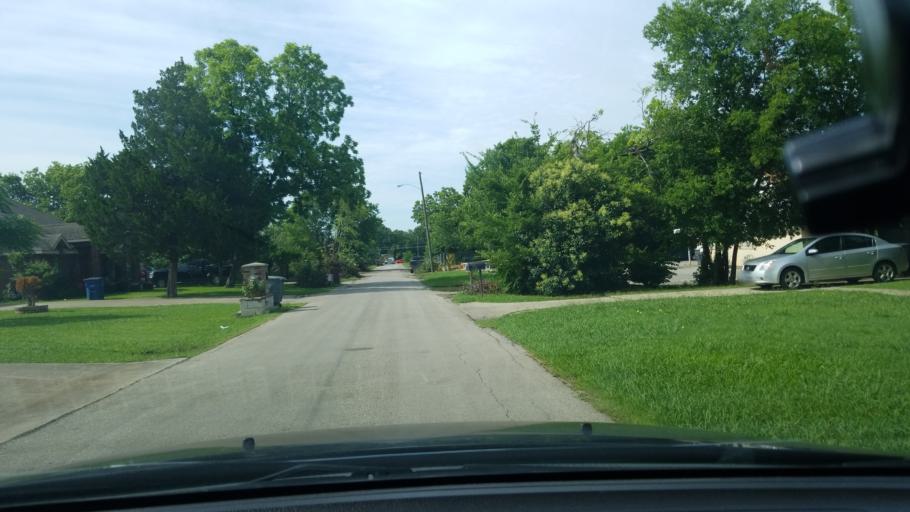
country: US
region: Texas
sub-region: Dallas County
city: Balch Springs
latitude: 32.7656
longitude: -96.6647
